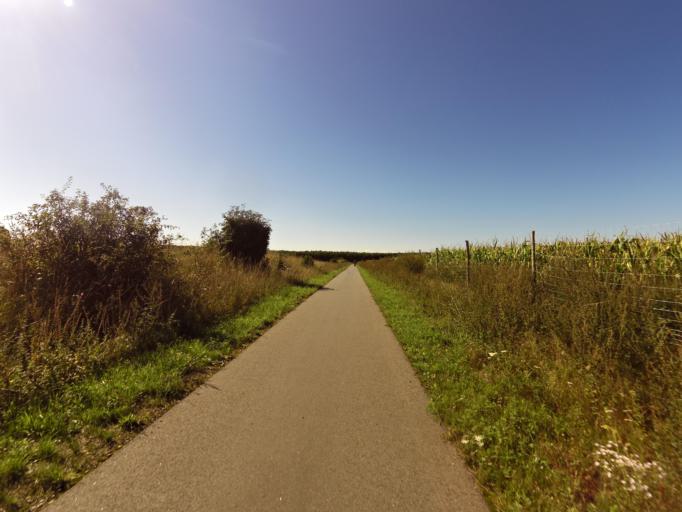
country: PL
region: West Pomeranian Voivodeship
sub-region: Powiat choszczenski
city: Pelczyce
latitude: 53.0152
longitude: 15.2822
